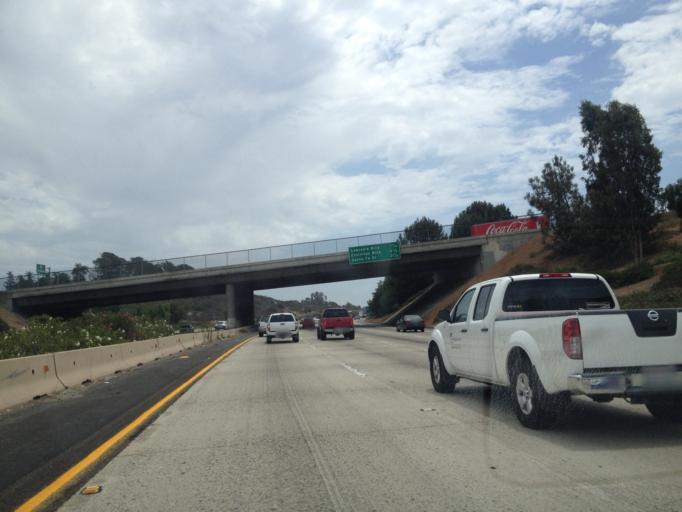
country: US
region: California
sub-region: San Diego County
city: Encinitas
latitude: 33.0851
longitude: -117.2987
